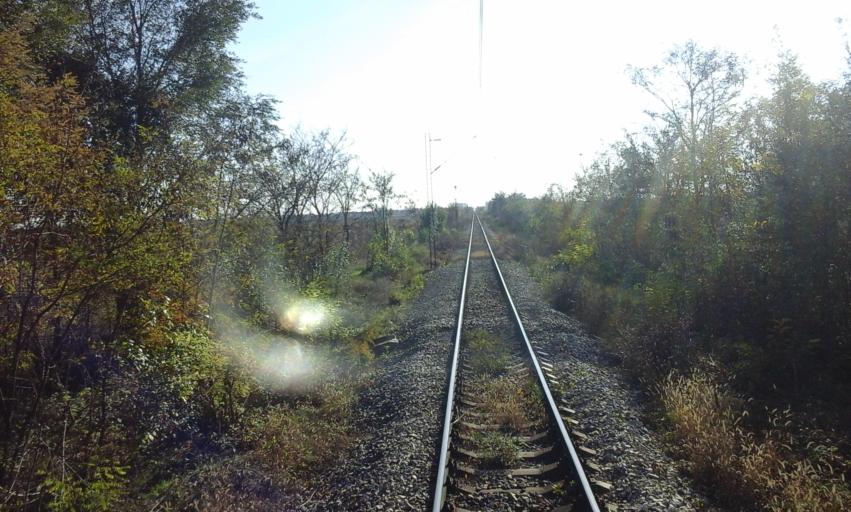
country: RS
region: Autonomna Pokrajina Vojvodina
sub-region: Severnobacki Okrug
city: Backa Topola
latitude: 45.8431
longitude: 19.6534
